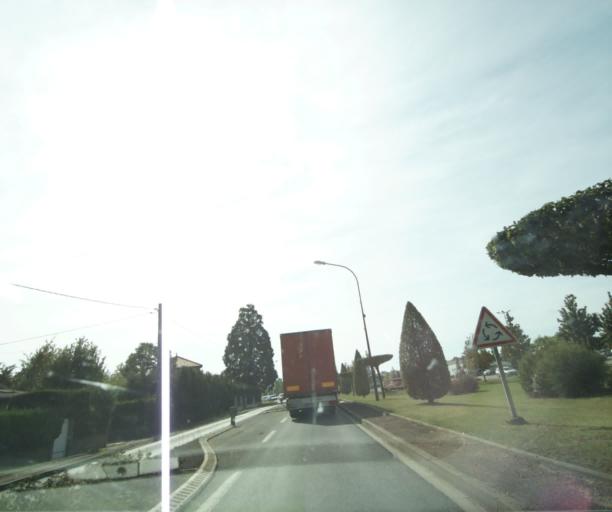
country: FR
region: Auvergne
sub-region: Departement de l'Allier
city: Saint-Remy-en-Rollat
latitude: 46.1584
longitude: 3.3932
